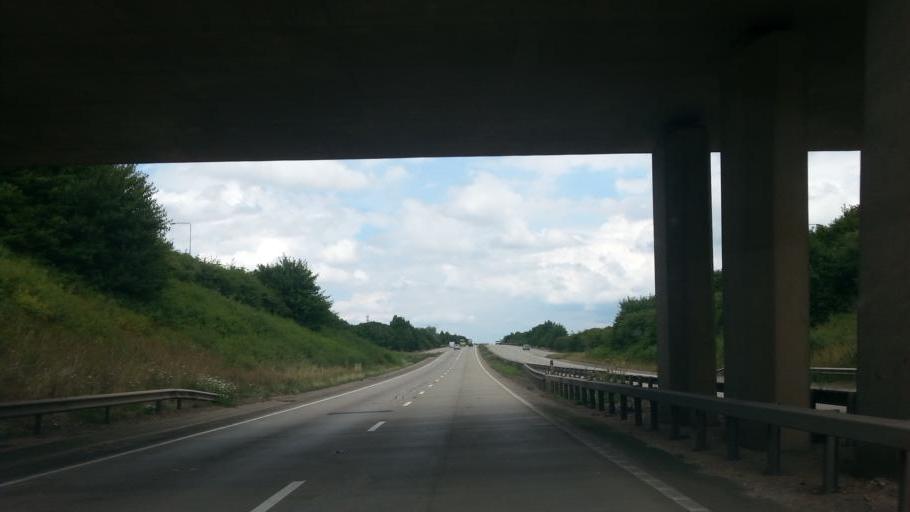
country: GB
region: England
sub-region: Norfolk
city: Hethersett
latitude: 52.5679
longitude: 1.1355
